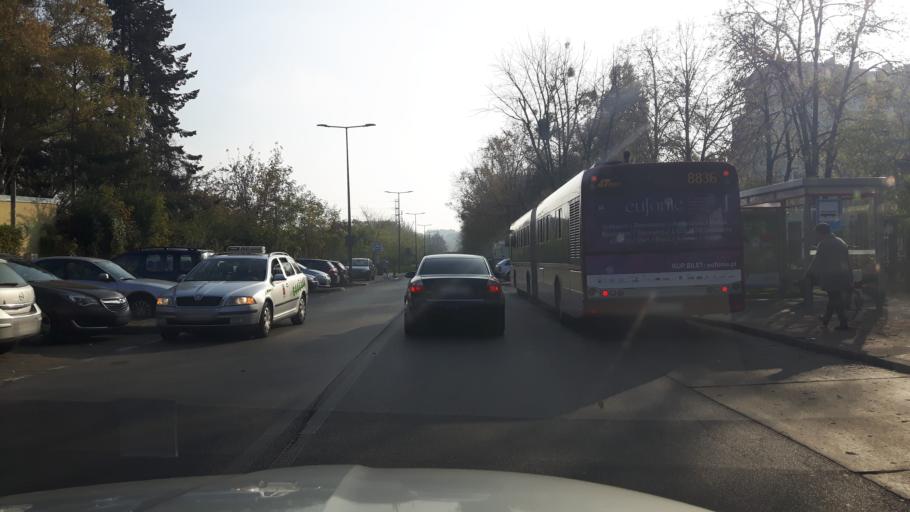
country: PL
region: Masovian Voivodeship
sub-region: Warszawa
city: Ochota
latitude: 52.1916
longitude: 20.9955
